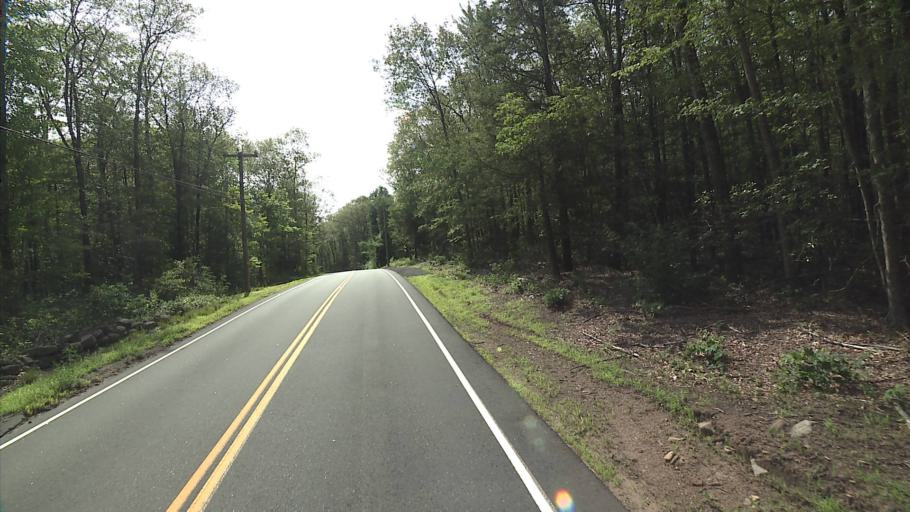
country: US
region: Massachusetts
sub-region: Hampden County
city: Holland
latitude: 41.9864
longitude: -72.1207
